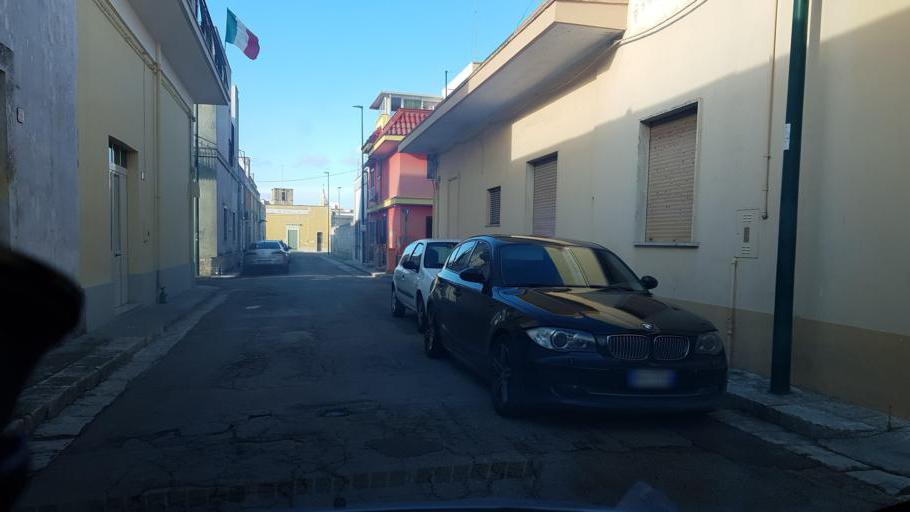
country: IT
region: Apulia
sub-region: Provincia di Lecce
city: Guagnano
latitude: 40.3992
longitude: 17.9513
